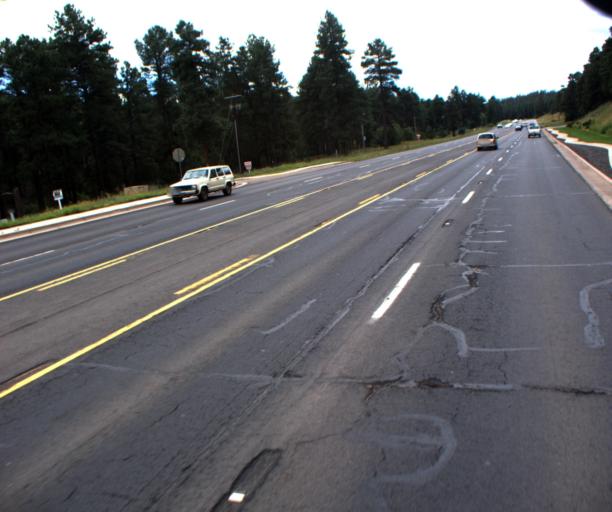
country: US
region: Arizona
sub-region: Navajo County
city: Show Low
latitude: 34.2306
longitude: -110.0271
